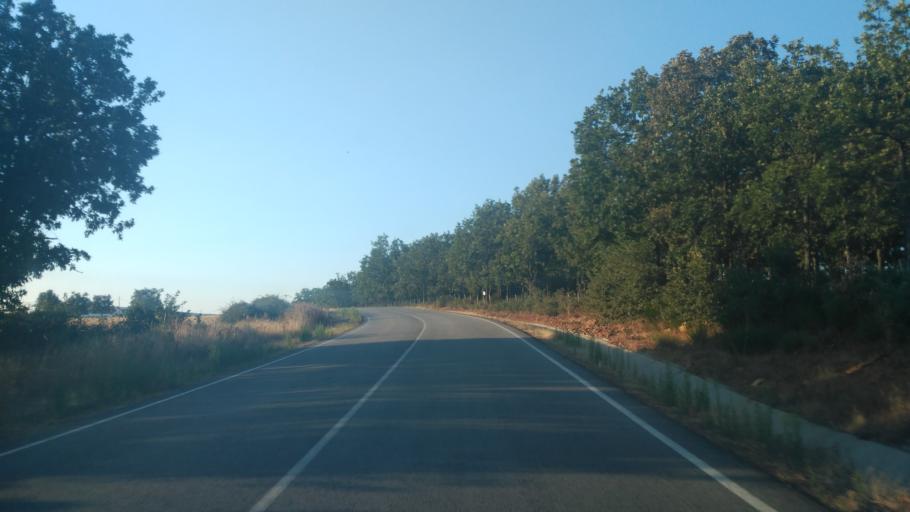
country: ES
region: Castille and Leon
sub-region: Provincia de Salamanca
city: Aldeanueva de la Sierra
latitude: 40.5981
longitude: -6.1361
